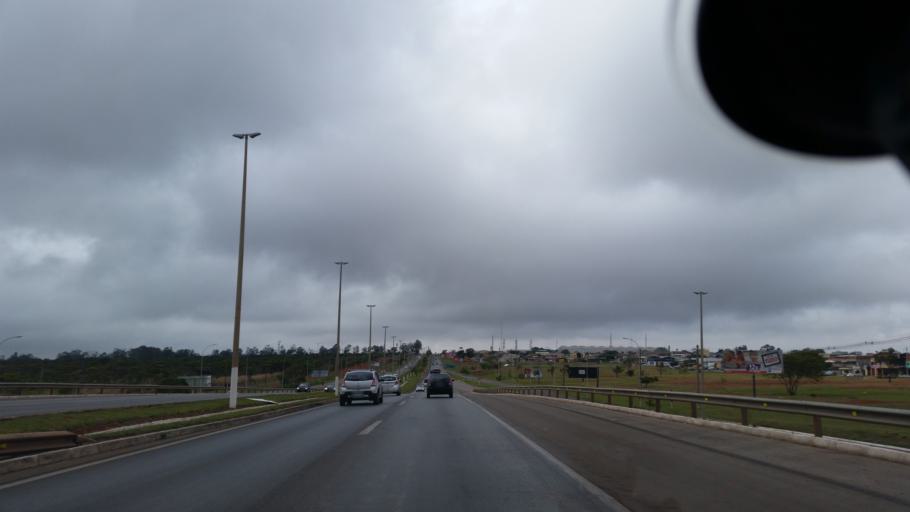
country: BR
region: Federal District
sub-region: Brasilia
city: Brasilia
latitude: -16.0039
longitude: -47.9841
